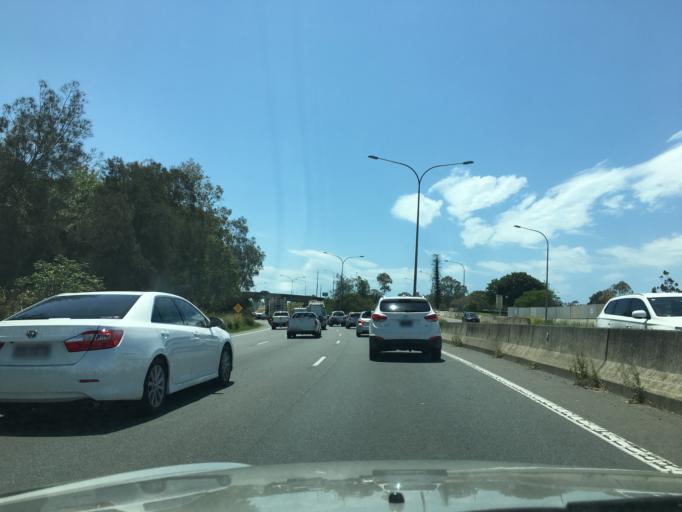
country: AU
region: Queensland
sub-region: Brisbane
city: Shorncliffe
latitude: -27.3757
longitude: 153.0964
